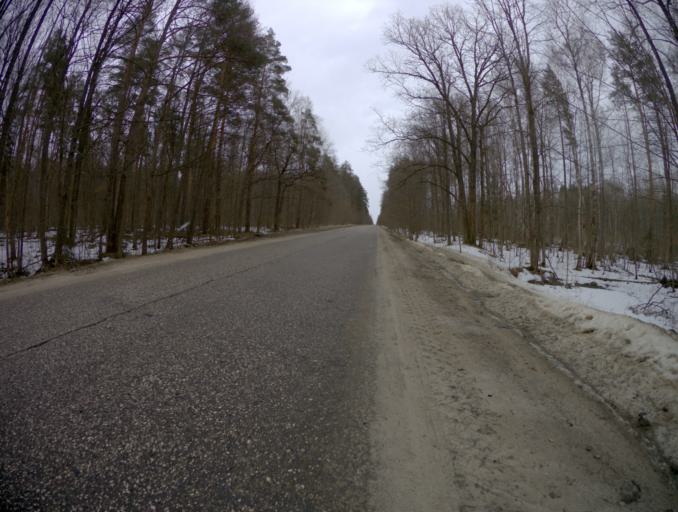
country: RU
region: Vladimir
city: Bogolyubovo
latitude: 56.1533
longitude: 40.5649
